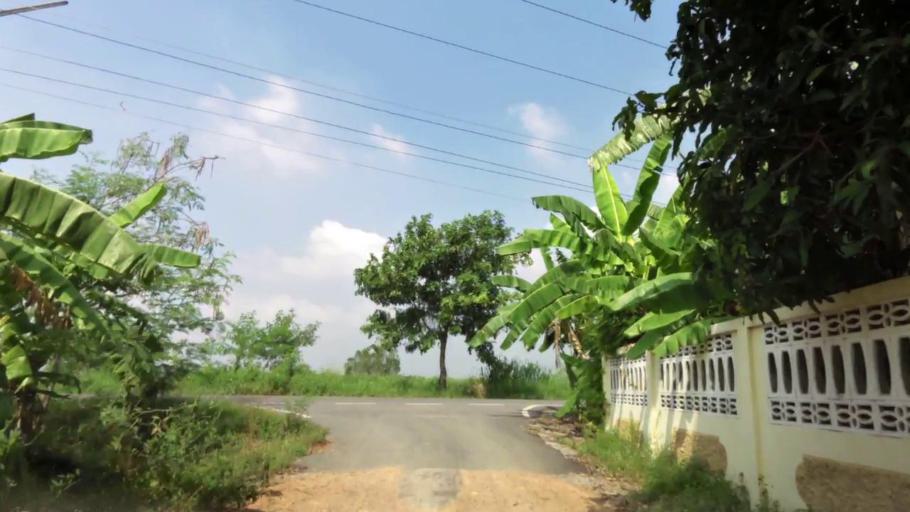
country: TH
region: Ang Thong
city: Pho Thong
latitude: 14.6215
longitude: 100.3976
